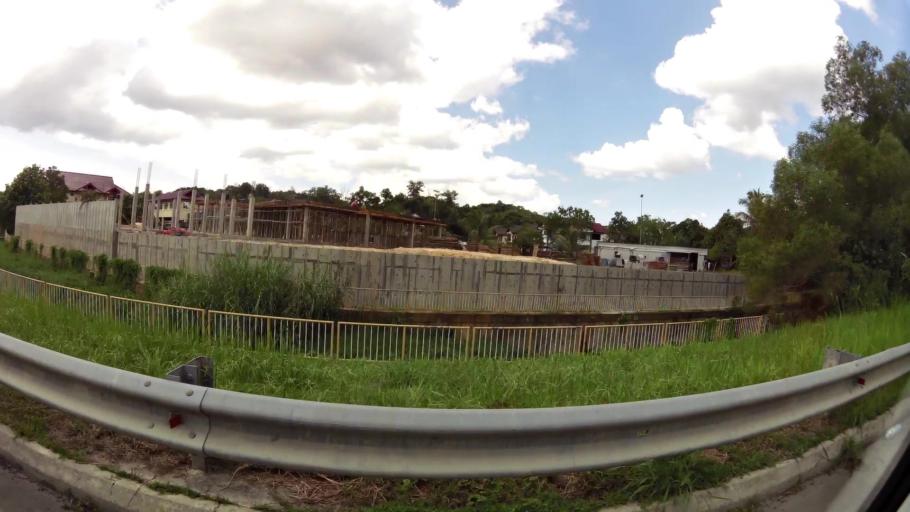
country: BN
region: Brunei and Muara
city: Bandar Seri Begawan
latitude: 4.9424
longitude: 114.9665
